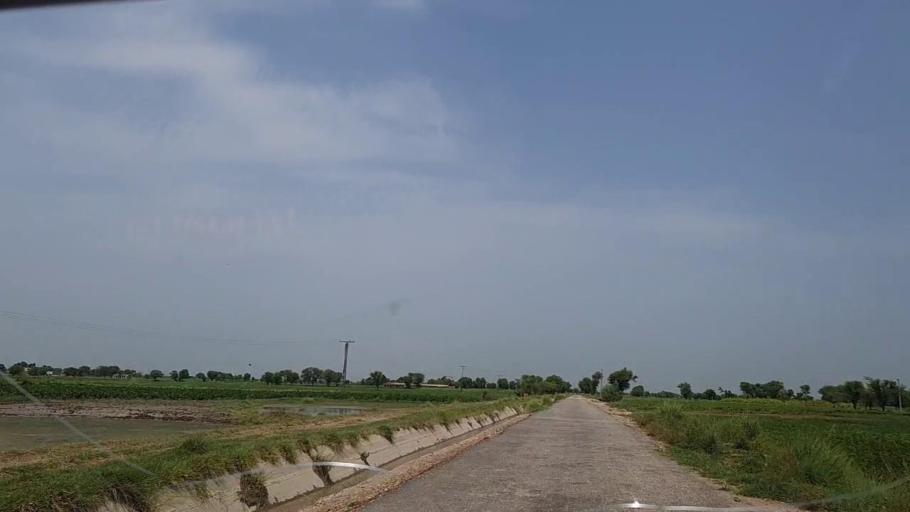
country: PK
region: Sindh
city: Tharu Shah
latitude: 26.9323
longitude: 68.0684
